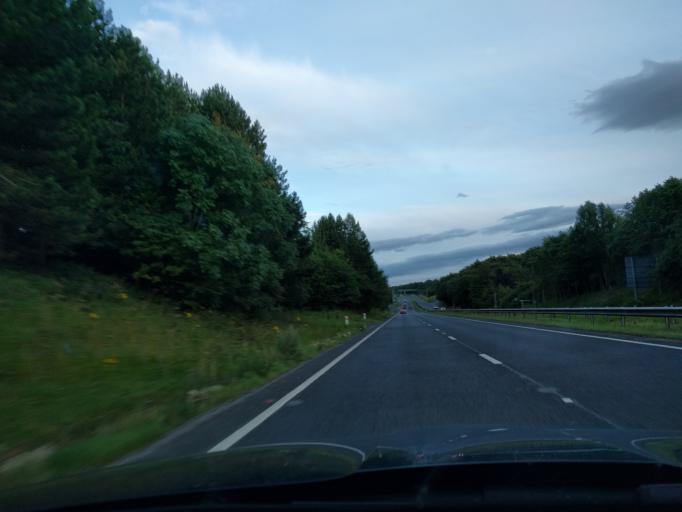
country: GB
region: England
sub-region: Northumberland
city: Stannington
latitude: 55.1013
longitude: -1.6624
